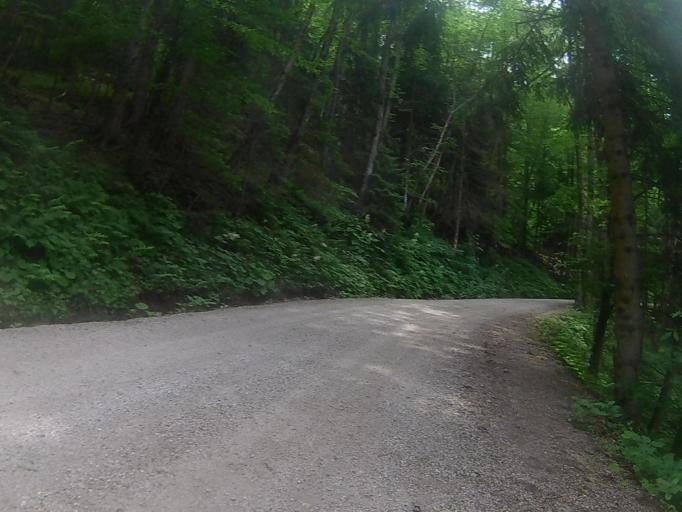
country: SI
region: Ruse
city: Ruse
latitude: 46.5249
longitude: 15.5377
